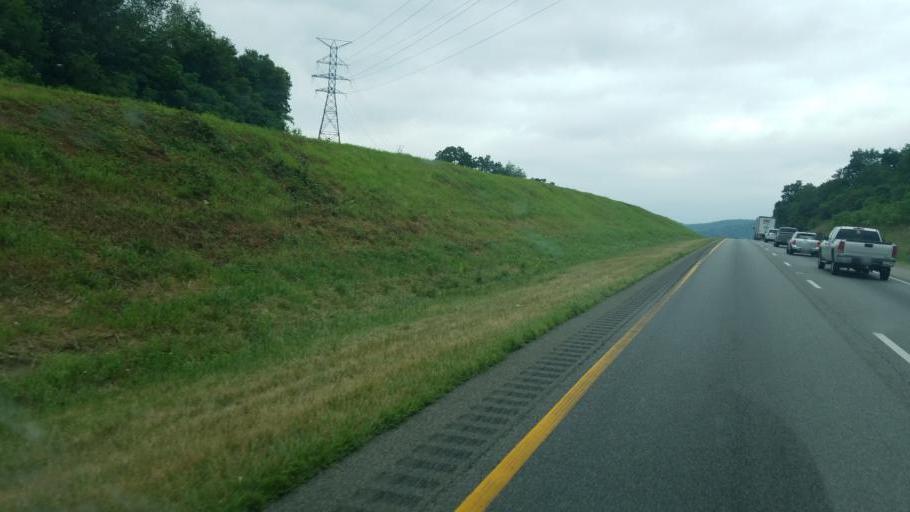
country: US
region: Virginia
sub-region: Wythe County
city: Wytheville
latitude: 36.9387
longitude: -80.9156
